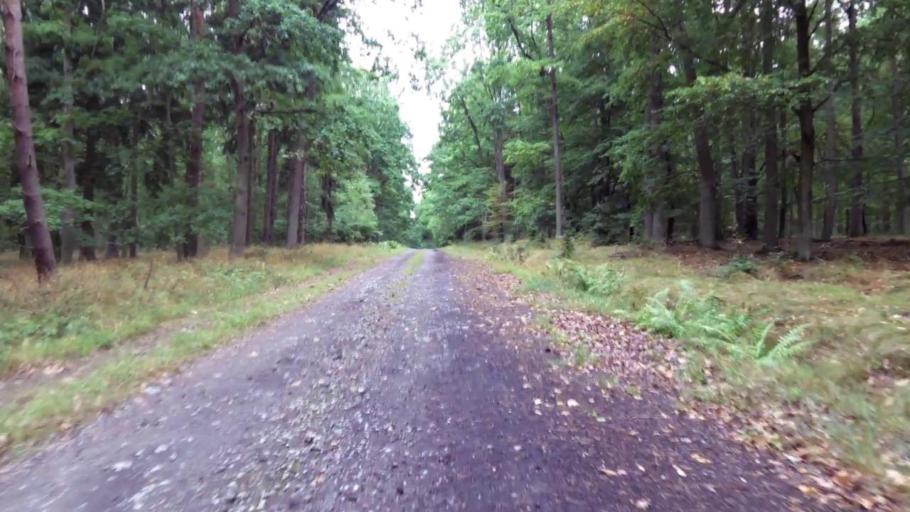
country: PL
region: West Pomeranian Voivodeship
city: Trzcinsko Zdroj
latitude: 52.8770
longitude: 14.6838
